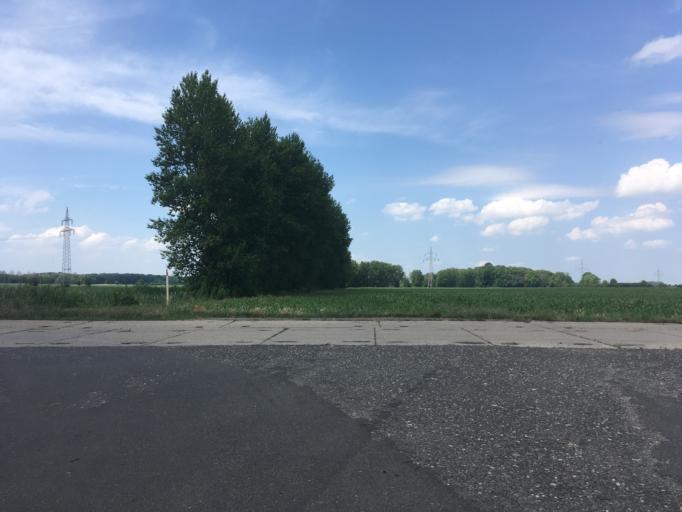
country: DE
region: Saxony-Anhalt
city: Osternienburg
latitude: 51.7629
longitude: 12.0626
